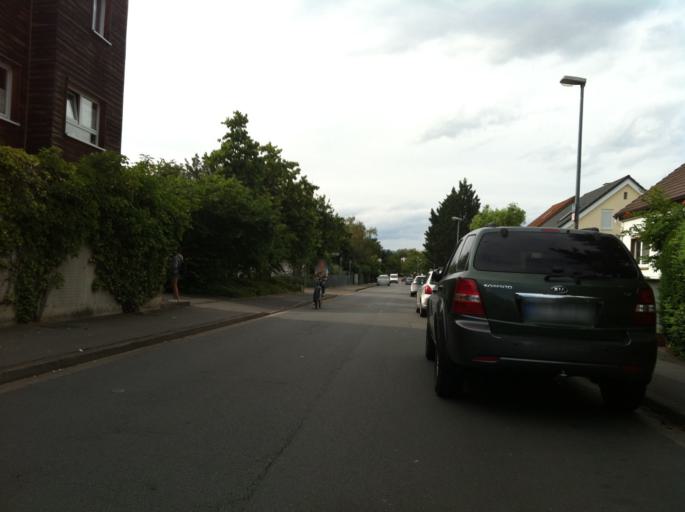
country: DE
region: Rheinland-Pfalz
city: Budenheim
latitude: 50.0066
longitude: 8.2130
